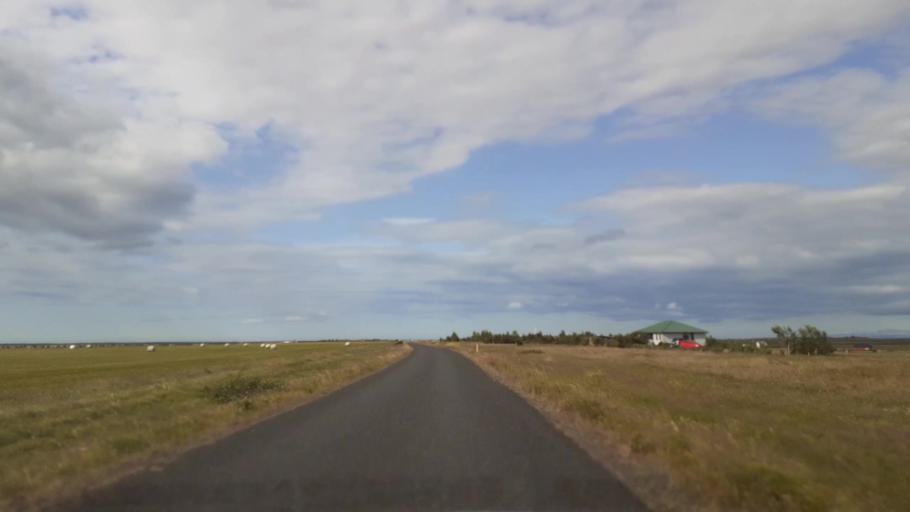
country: IS
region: South
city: Vestmannaeyjar
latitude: 63.7702
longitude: -20.2905
